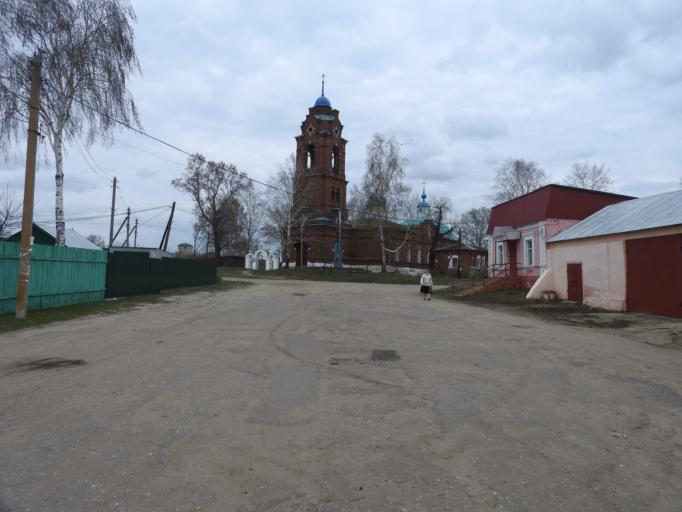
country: RU
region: Rjazan
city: Shilovo
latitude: 54.3769
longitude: 40.7626
